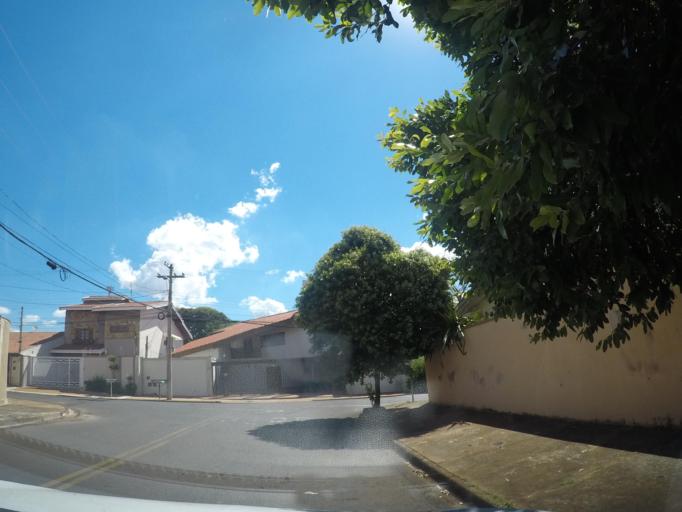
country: BR
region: Sao Paulo
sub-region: Sumare
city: Sumare
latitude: -22.8310
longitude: -47.2694
